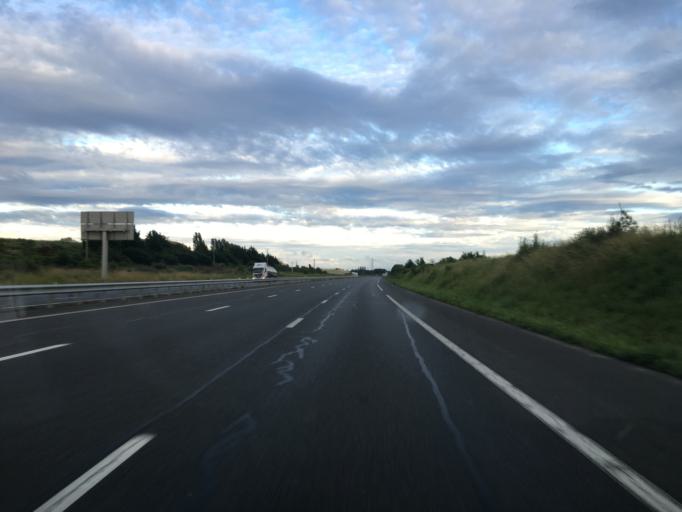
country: FR
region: Ile-de-France
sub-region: Departement de Seine-et-Marne
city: Moisenay
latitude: 48.5792
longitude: 2.7409
